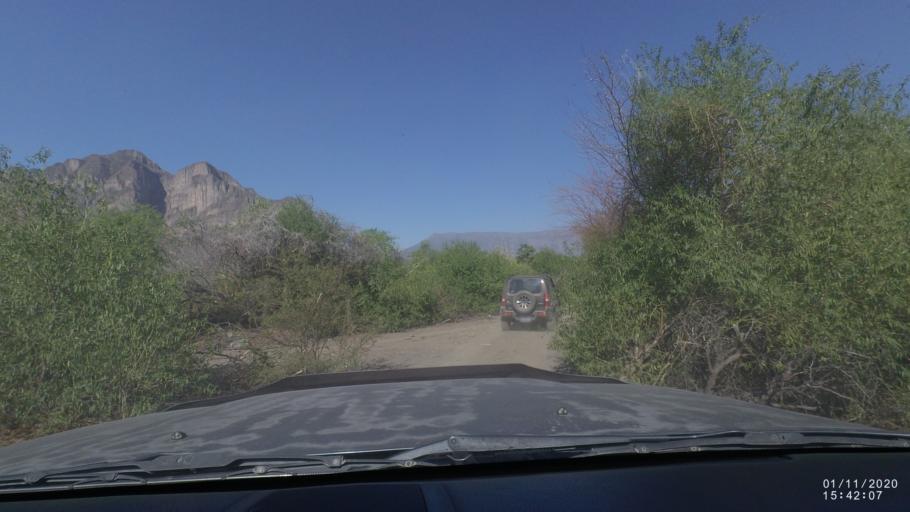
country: BO
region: Chuquisaca
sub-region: Provincia Zudanez
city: Mojocoya
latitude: -18.6780
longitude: -64.5011
